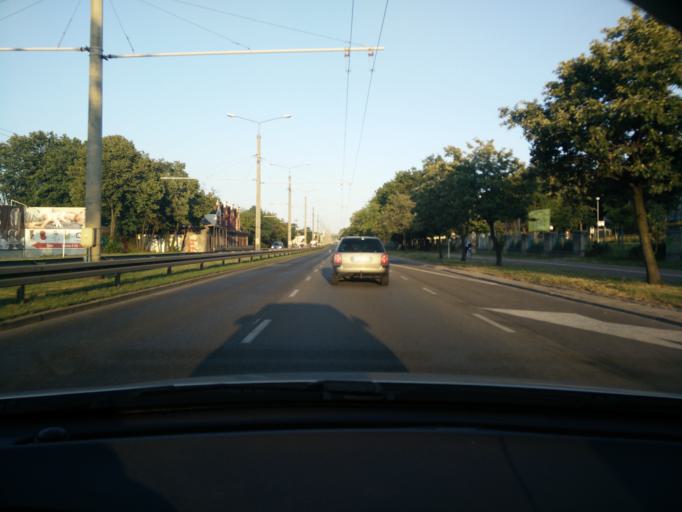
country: PL
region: Pomeranian Voivodeship
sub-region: Gdynia
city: Gdynia
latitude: 54.5260
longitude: 18.5136
